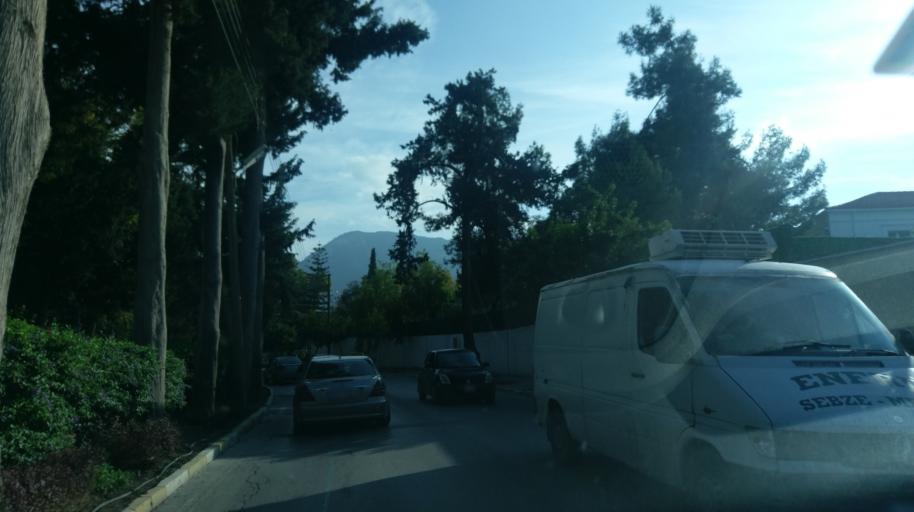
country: CY
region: Keryneia
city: Kyrenia
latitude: 35.3357
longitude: 33.3261
